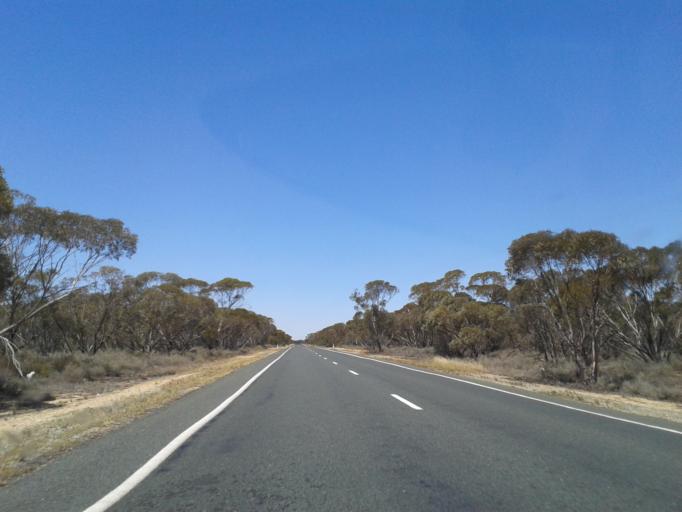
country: AU
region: New South Wales
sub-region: Wentworth
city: Gol Gol
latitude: -34.5237
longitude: 142.6186
